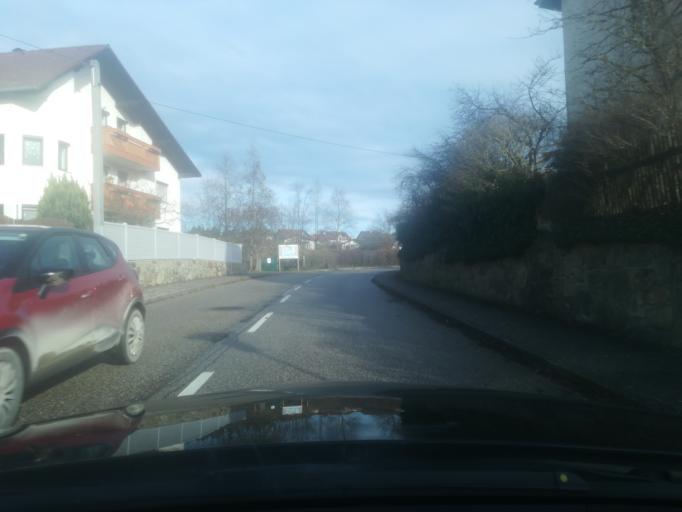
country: AT
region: Upper Austria
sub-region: Politischer Bezirk Perg
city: Perg
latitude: 48.3347
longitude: 14.6222
